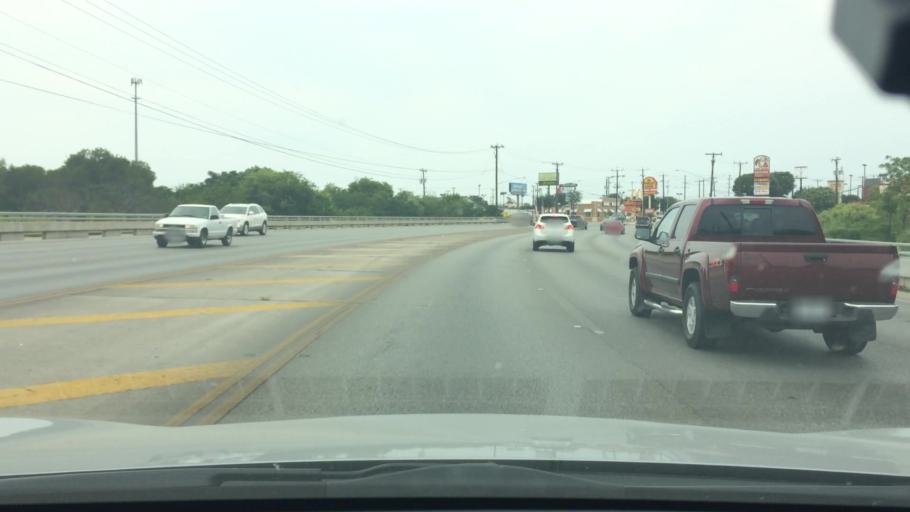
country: US
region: Texas
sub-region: Bexar County
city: Leon Valley
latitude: 29.4817
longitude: -98.6671
